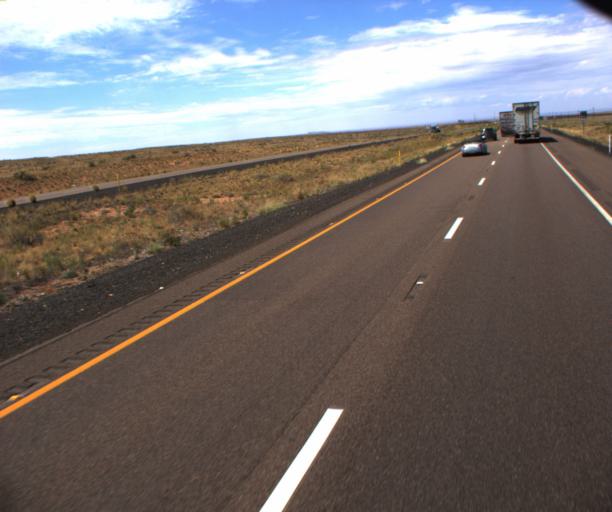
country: US
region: Arizona
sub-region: Navajo County
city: Holbrook
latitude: 35.0545
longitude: -109.7919
